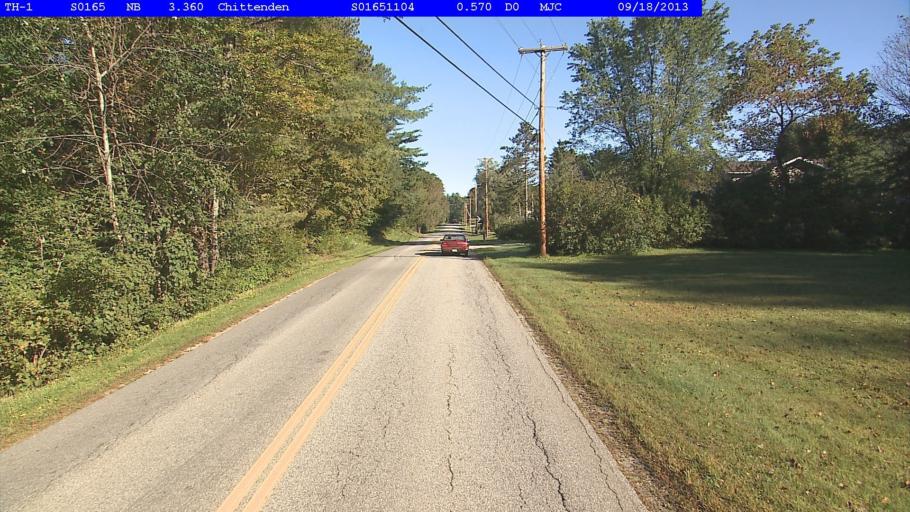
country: US
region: Vermont
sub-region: Rutland County
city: Rutland
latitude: 43.6852
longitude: -72.9504
